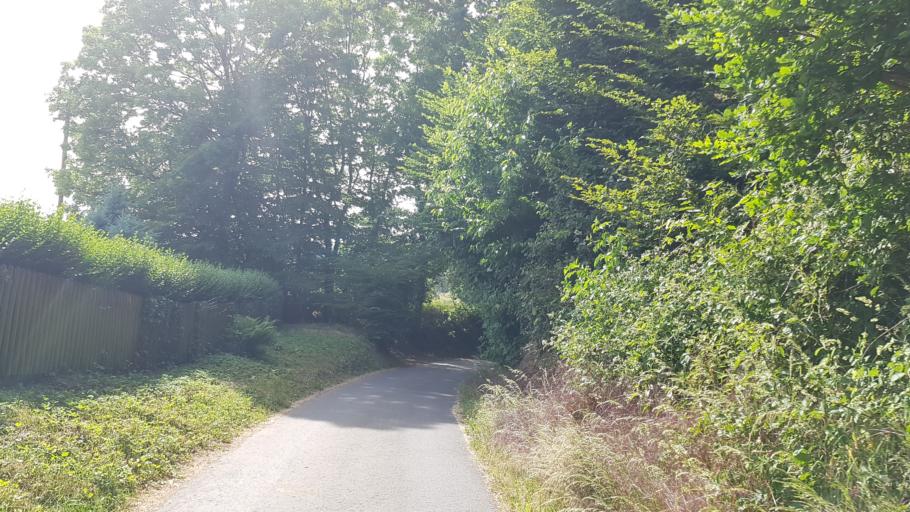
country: DE
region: North Rhine-Westphalia
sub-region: Regierungsbezirk Dusseldorf
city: Muelheim (Ruhr)
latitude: 51.4005
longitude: 6.9037
